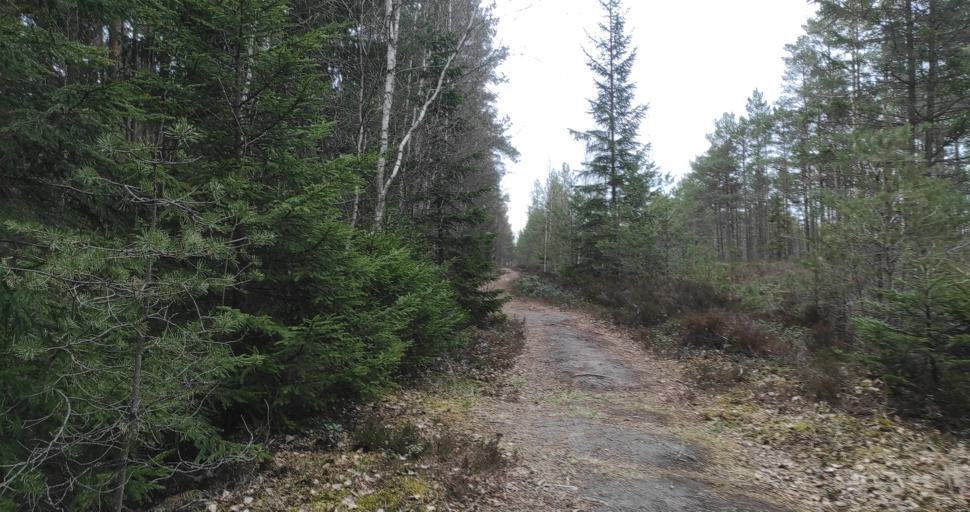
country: LV
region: Dundaga
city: Dundaga
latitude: 57.3459
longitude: 22.1498
